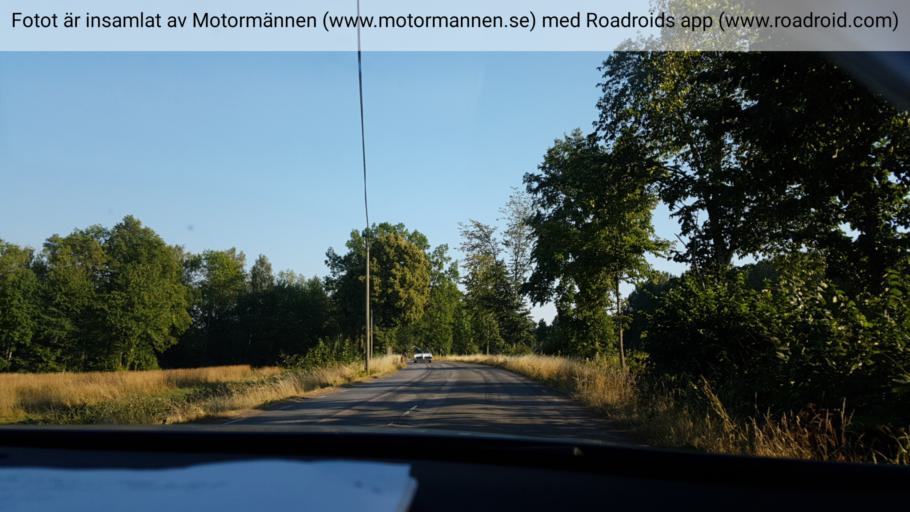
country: SE
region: Vaestra Goetaland
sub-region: Skovde Kommun
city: Stopen
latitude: 58.4796
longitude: 13.8386
